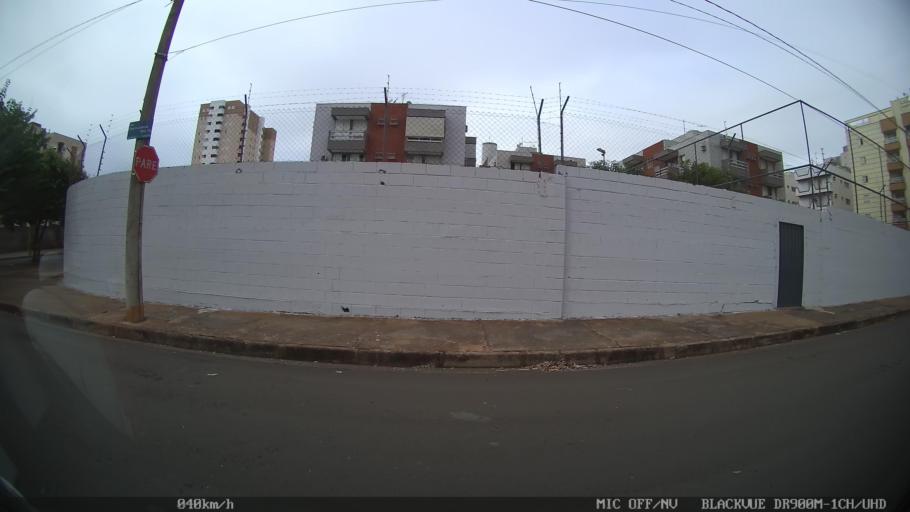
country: BR
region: Sao Paulo
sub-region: Sao Jose Do Rio Preto
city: Sao Jose do Rio Preto
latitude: -20.8319
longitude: -49.3896
